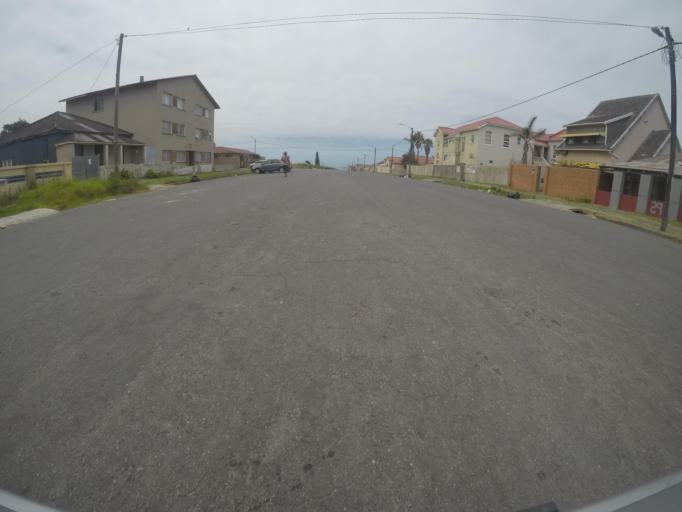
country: ZA
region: Eastern Cape
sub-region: Buffalo City Metropolitan Municipality
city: East London
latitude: -33.0152
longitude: 27.9135
